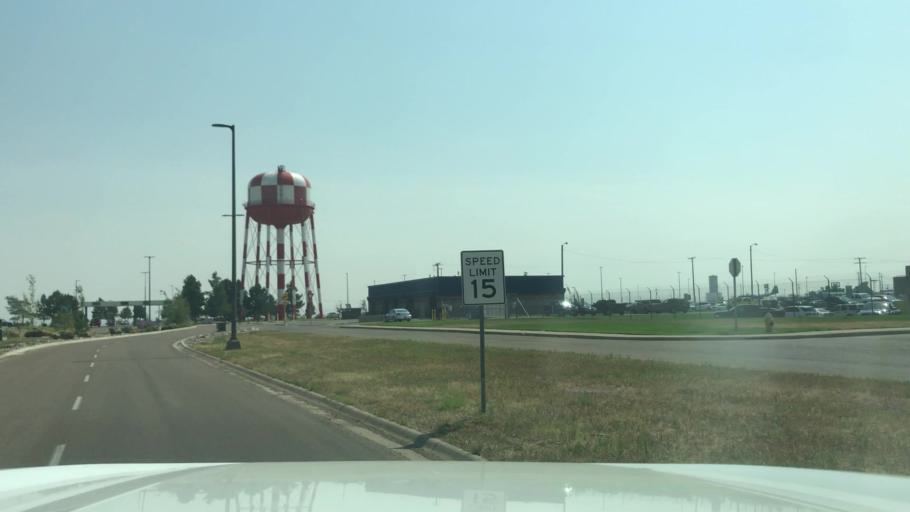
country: US
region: Montana
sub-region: Cascade County
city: Great Falls
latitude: 47.4810
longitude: -111.3593
